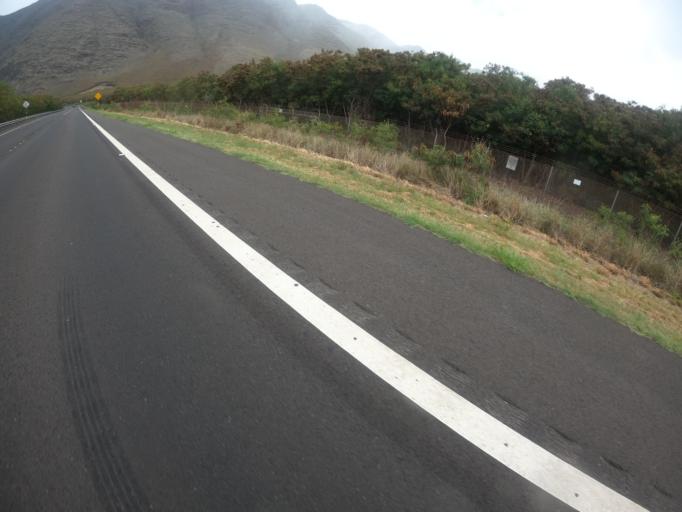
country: US
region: Hawaii
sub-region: Honolulu County
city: Makaha Valley
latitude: 21.5326
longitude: -158.2281
